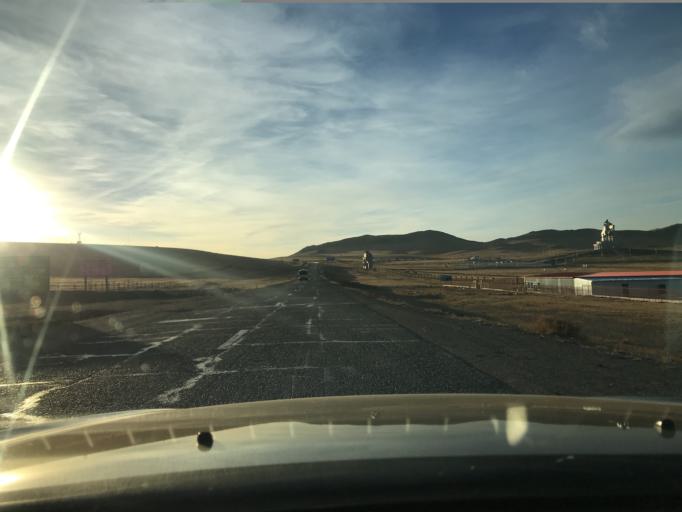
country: MN
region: Central Aimak
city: Arhust
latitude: 47.8042
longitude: 107.5395
